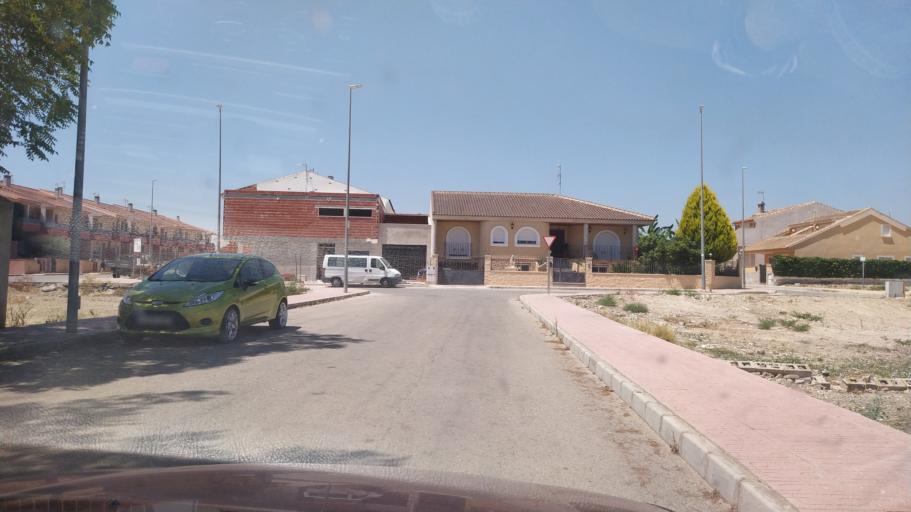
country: ES
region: Murcia
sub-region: Murcia
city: Ceuti
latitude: 38.0850
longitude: -1.2754
